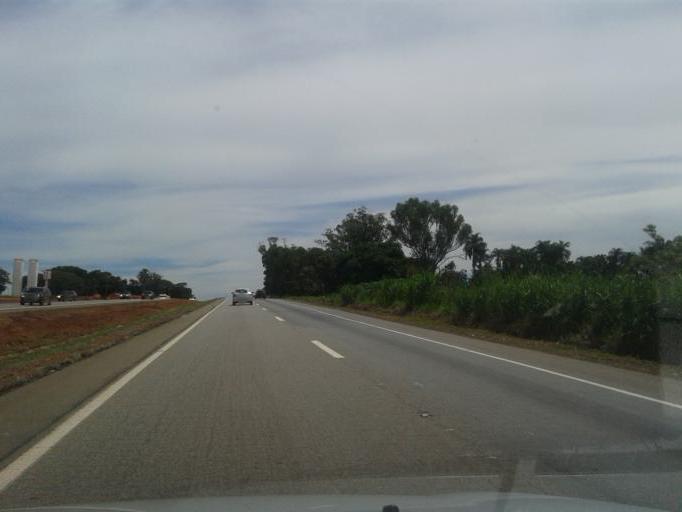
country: BR
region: Goias
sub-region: Hidrolandia
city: Hidrolandia
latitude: -17.0443
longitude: -49.2254
